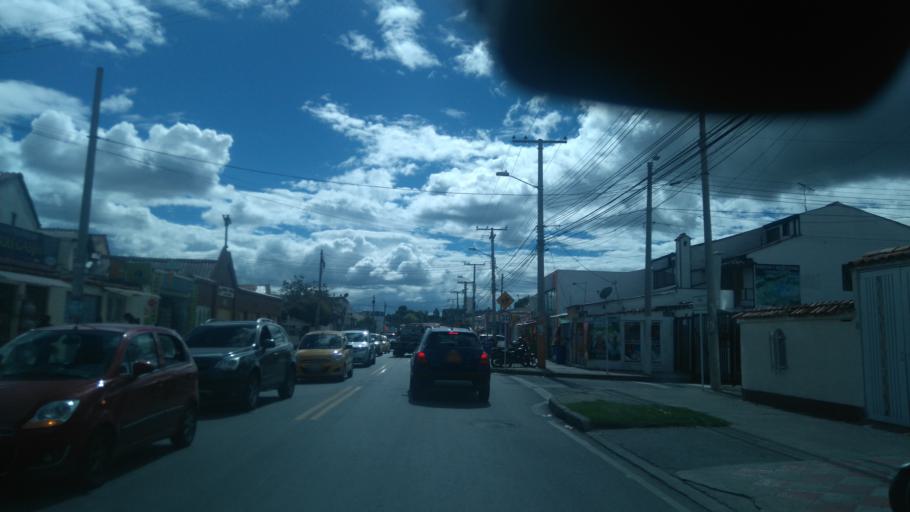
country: CO
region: Cundinamarca
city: Cota
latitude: 4.7564
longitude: -74.0522
